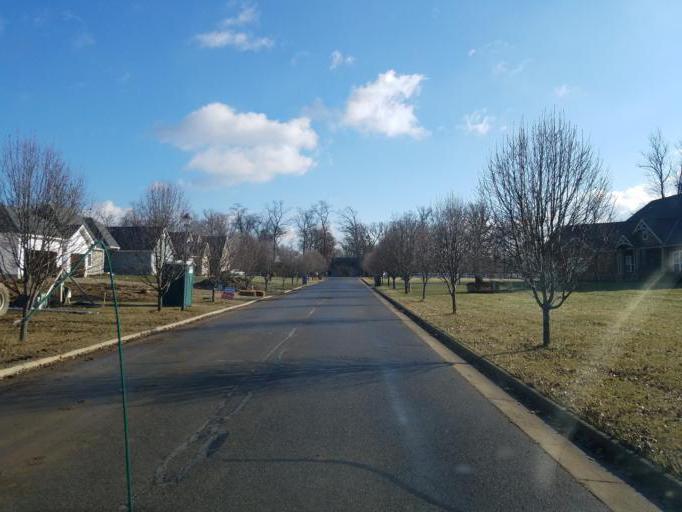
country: US
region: Ohio
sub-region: Marion County
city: Marion
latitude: 40.5425
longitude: -83.1572
